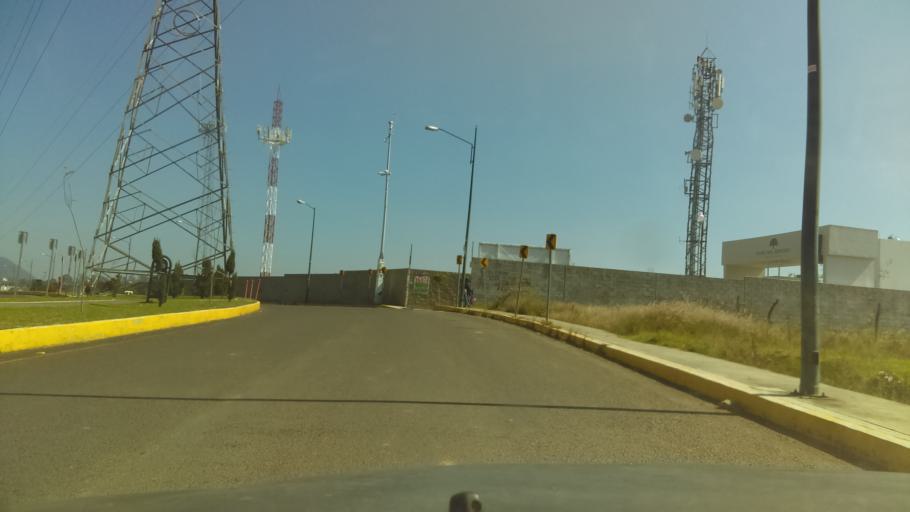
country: MX
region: Michoacan
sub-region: Morelia
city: Montana Monarca (Punta Altozano)
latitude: 19.6581
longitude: -101.1748
